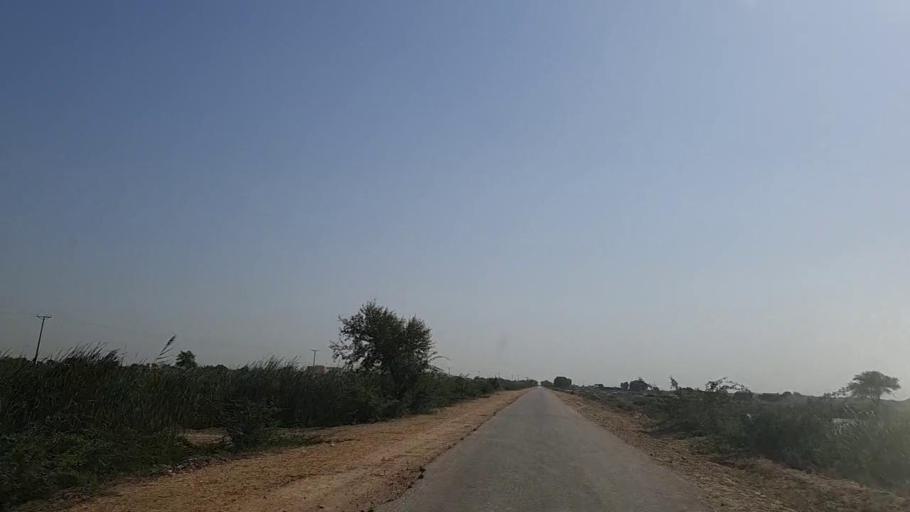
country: PK
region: Sindh
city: Mirpur Batoro
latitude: 24.6462
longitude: 68.2895
